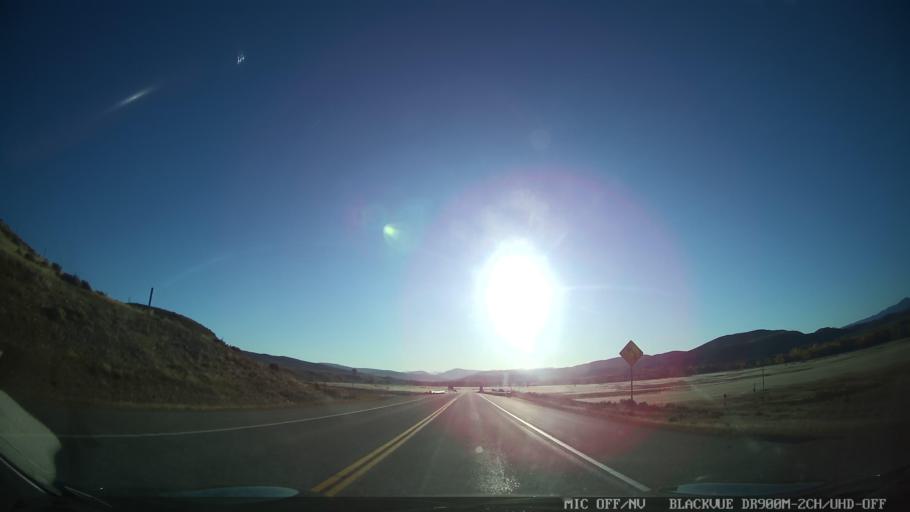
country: US
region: Colorado
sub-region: Grand County
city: Kremmling
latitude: 40.0651
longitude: -106.2853
